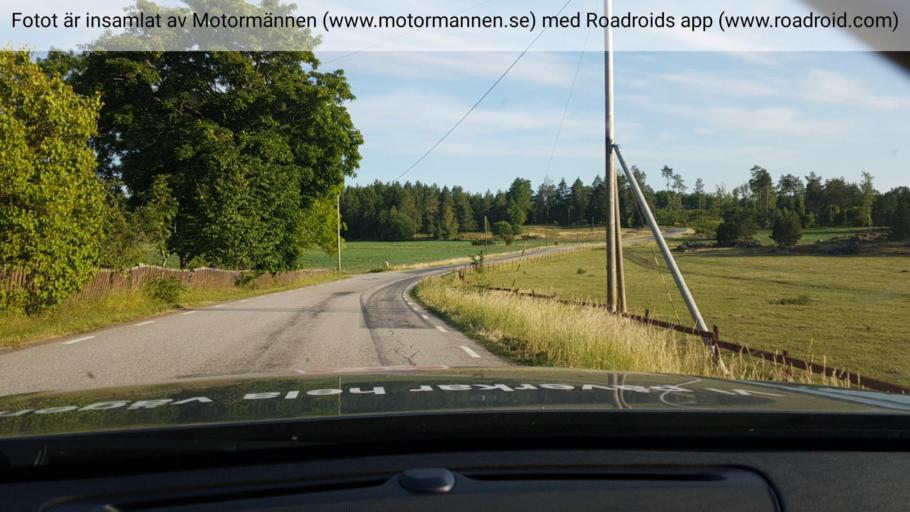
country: SE
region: Uppsala
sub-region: Osthammars Kommun
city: Gimo
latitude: 59.9989
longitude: 18.0598
